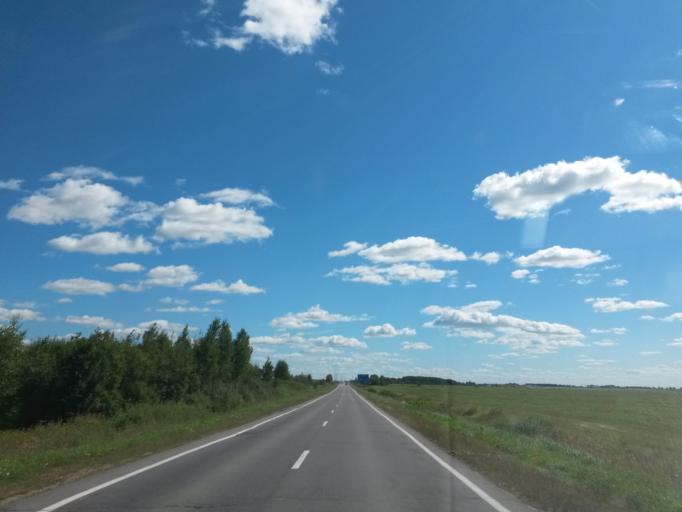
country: RU
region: Jaroslavl
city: Yaroslavl
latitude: 57.7464
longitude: 39.8830
